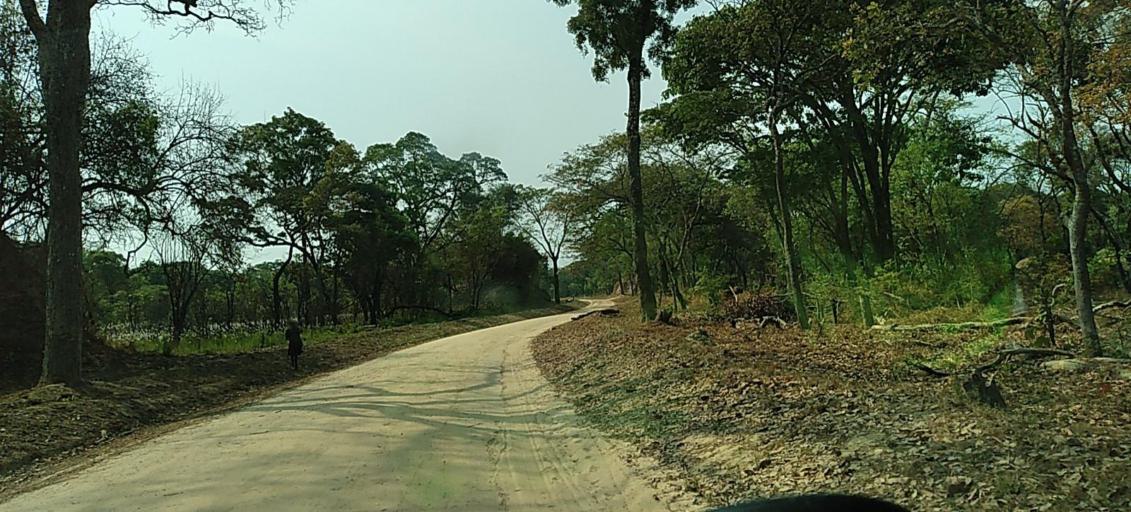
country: ZM
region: North-Western
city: Solwezi
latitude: -12.7040
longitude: 26.4156
